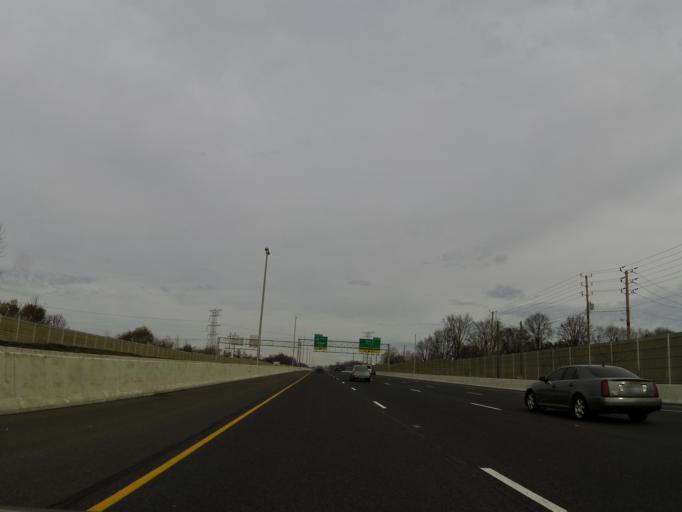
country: US
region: Indiana
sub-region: Marion County
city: Speedway
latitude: 39.8406
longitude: -86.2759
